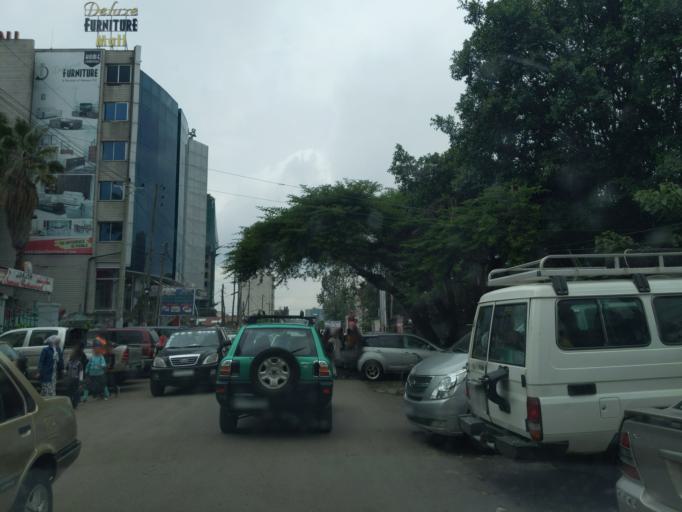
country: ET
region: Adis Abeba
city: Addis Ababa
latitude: 8.9994
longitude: 38.7678
